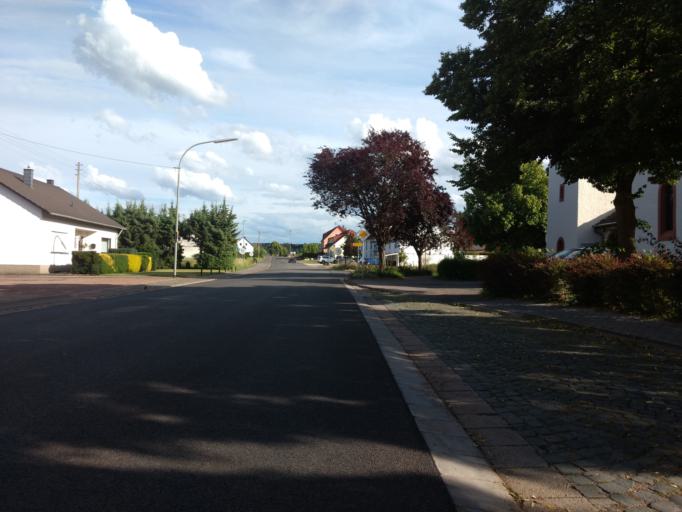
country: DE
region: Saarland
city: Merzig
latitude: 49.4502
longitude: 6.6036
